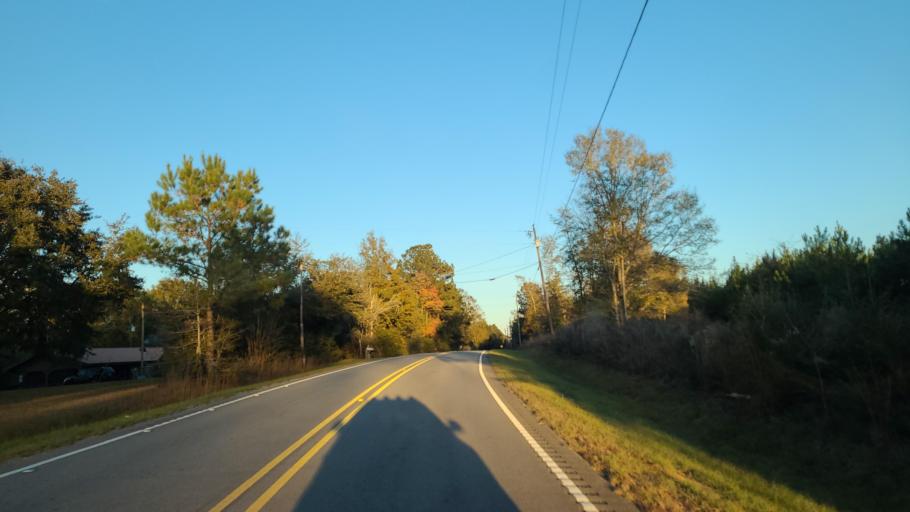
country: US
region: Mississippi
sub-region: Lamar County
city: Purvis
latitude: 31.0249
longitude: -89.2485
